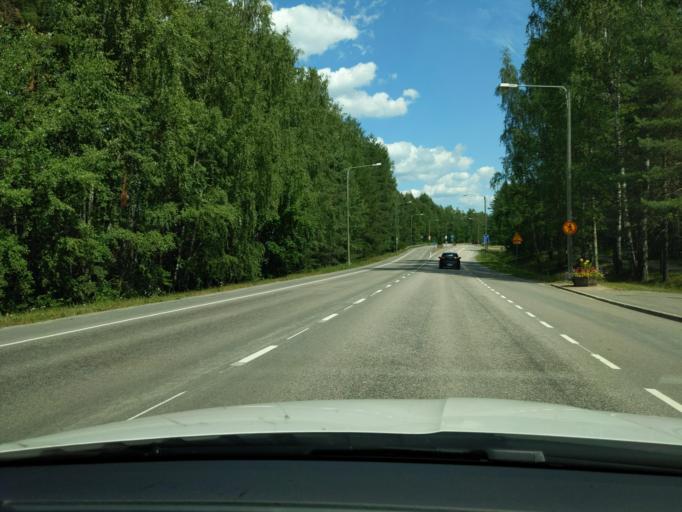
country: FI
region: Paijanne Tavastia
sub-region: Lahti
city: Heinola
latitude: 61.1950
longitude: 26.0152
